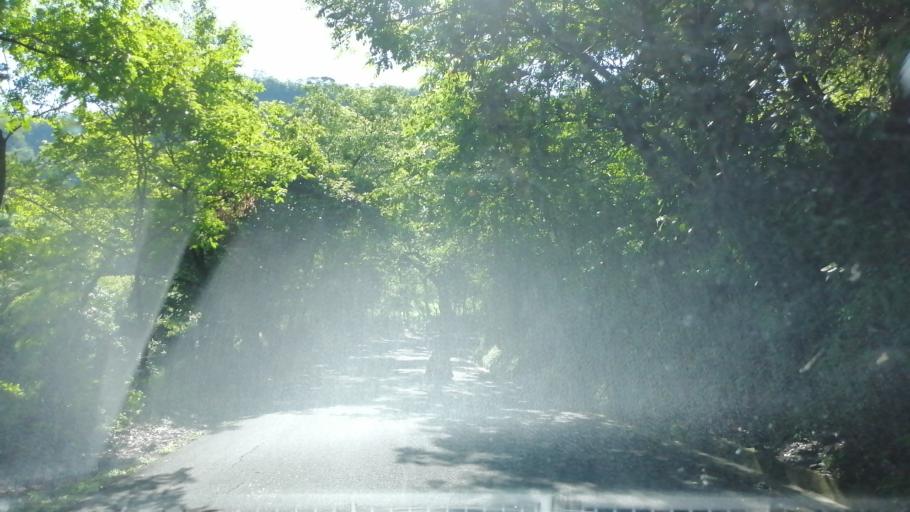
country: SV
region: Morazan
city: Cacaopera
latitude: 13.7695
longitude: -88.0710
